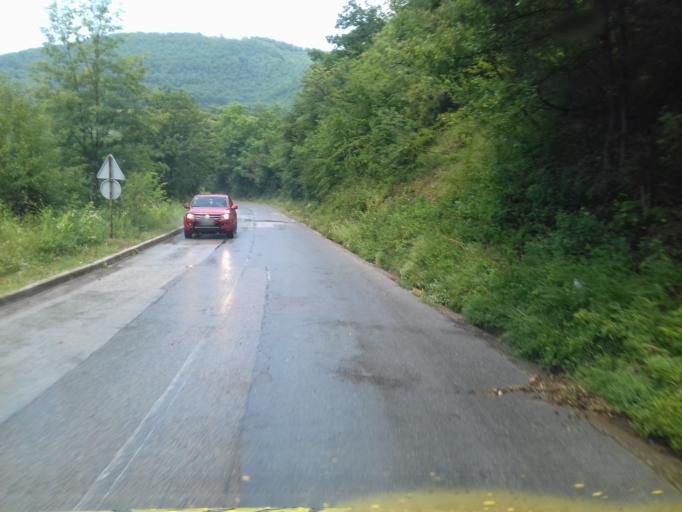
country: BA
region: Federation of Bosnia and Herzegovina
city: Kiseljak
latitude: 43.9547
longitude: 18.1167
